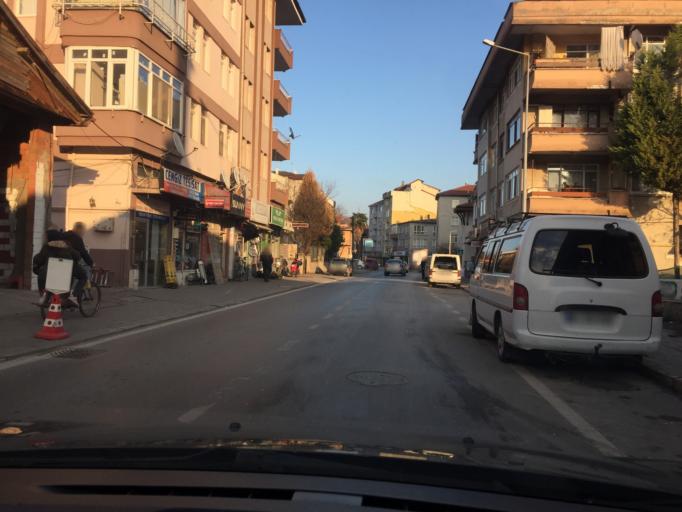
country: TR
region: Sakarya
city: Adapazari
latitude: 40.7832
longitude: 30.4002
